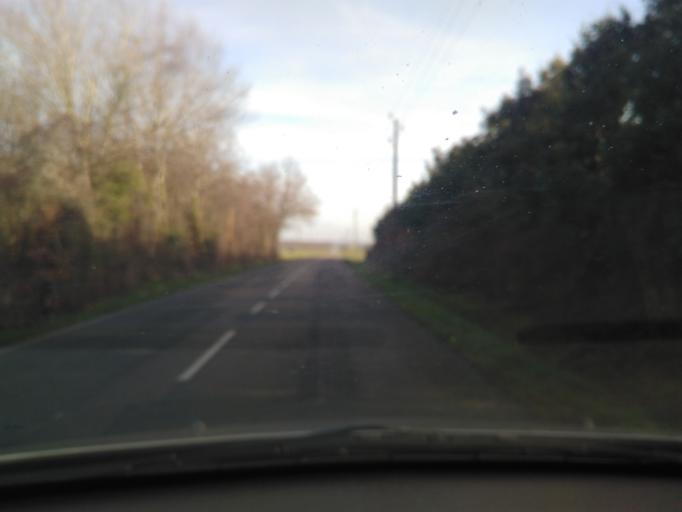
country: FR
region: Bourgogne
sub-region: Departement de la Nievre
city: Dornes
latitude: 46.7730
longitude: 3.3415
